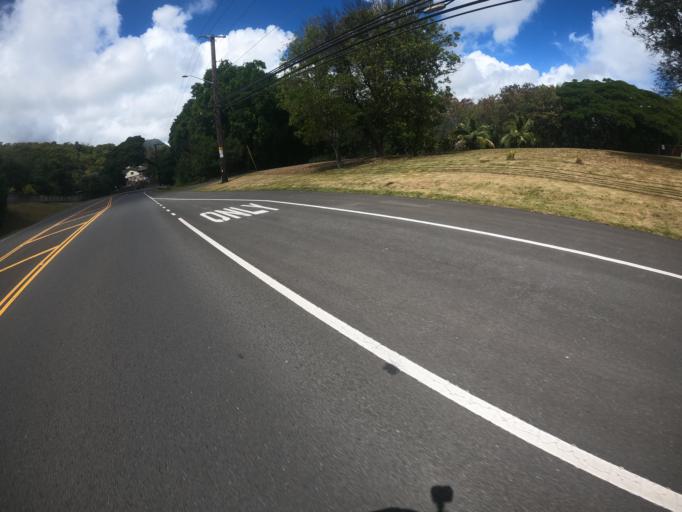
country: US
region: Hawaii
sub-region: Honolulu County
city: Kane'ohe
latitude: 21.4075
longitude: -157.7815
